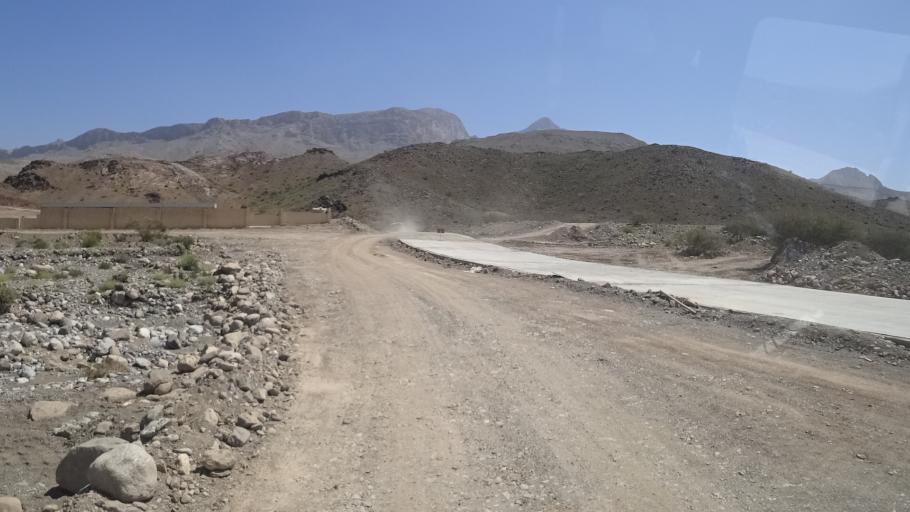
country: OM
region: Muhafazat ad Dakhiliyah
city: Bahla'
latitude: 23.2252
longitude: 57.0605
